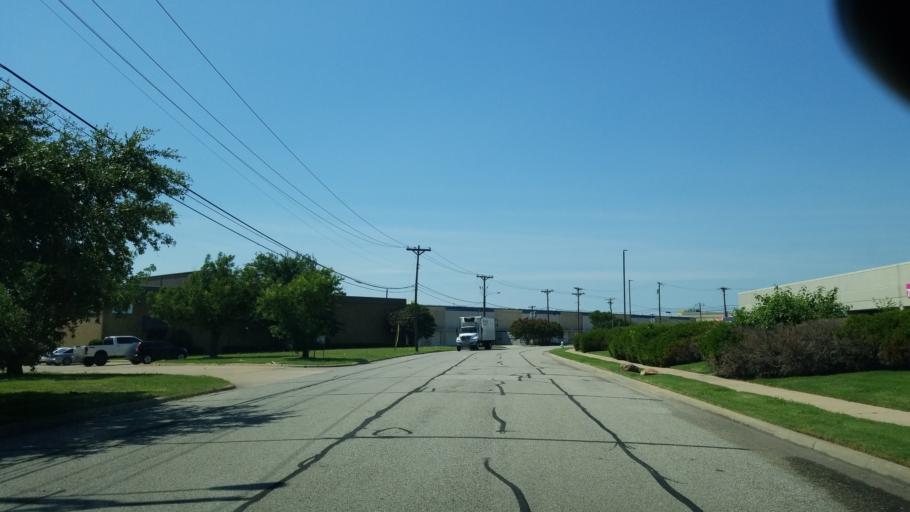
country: US
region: Texas
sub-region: Dallas County
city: Farmers Branch
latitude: 32.9249
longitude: -96.9035
